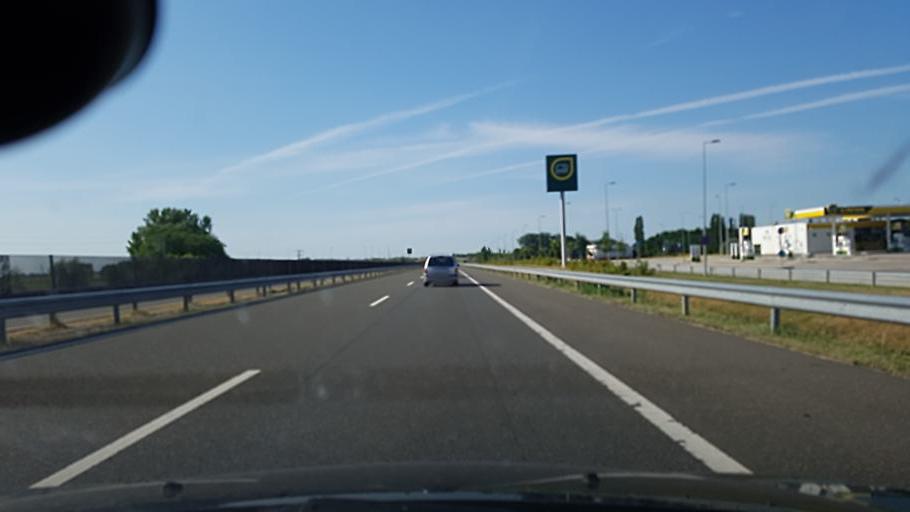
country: HU
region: Tolna
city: Paks
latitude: 46.6478
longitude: 18.8155
